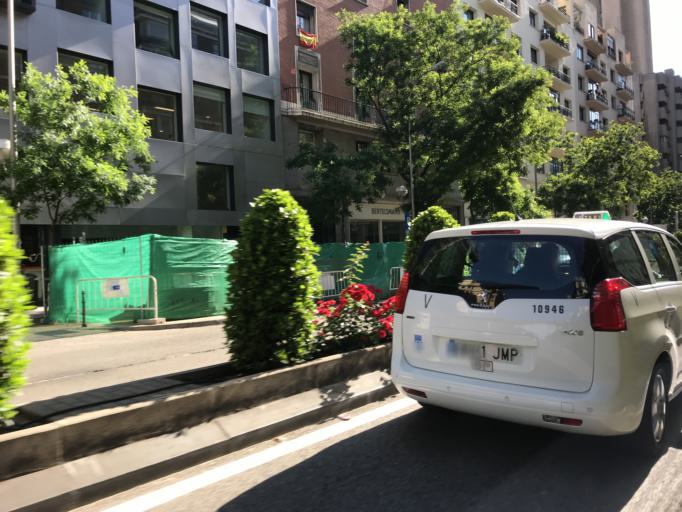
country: ES
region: Madrid
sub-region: Provincia de Madrid
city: Salamanca
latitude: 40.4214
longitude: -3.6777
